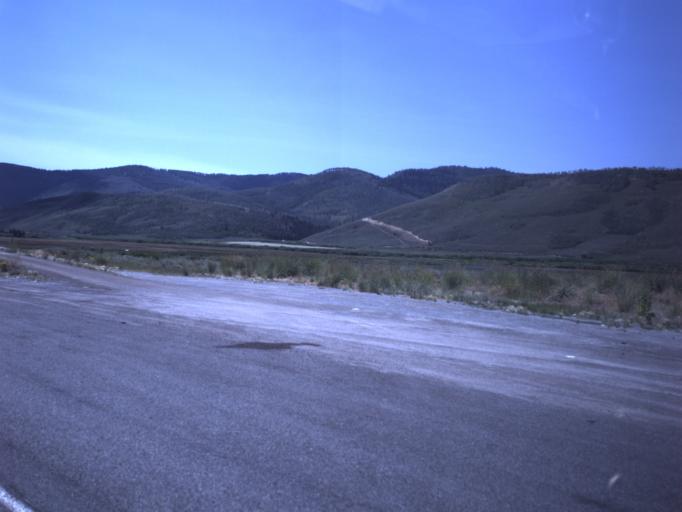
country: US
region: Utah
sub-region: Carbon County
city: Helper
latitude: 39.7500
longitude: -111.1505
